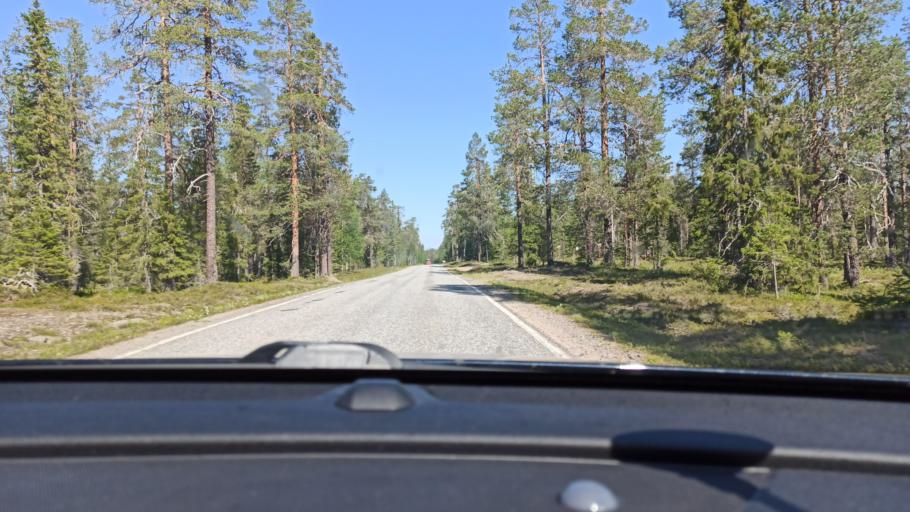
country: FI
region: Lapland
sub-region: Tunturi-Lappi
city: Kolari
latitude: 67.6619
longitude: 24.1648
